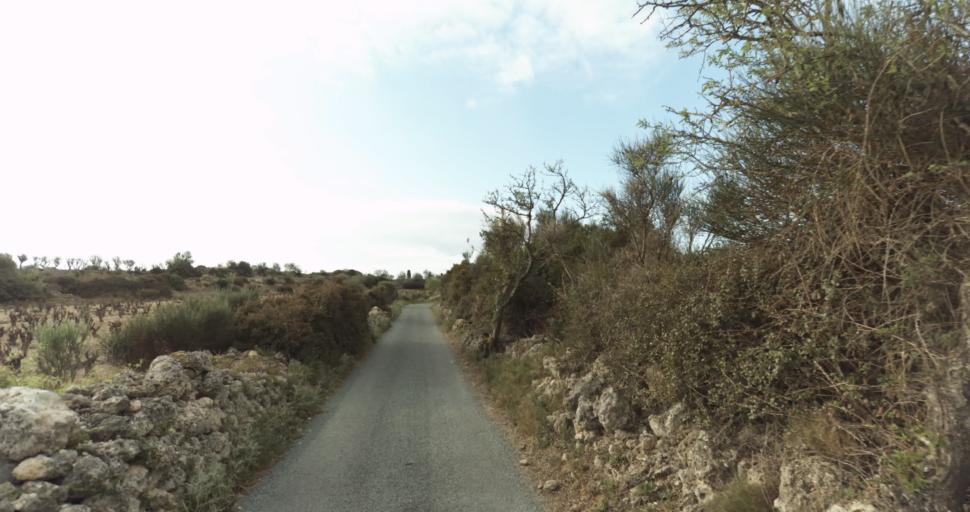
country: FR
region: Languedoc-Roussillon
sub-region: Departement de l'Aude
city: Leucate
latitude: 42.9253
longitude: 3.0281
